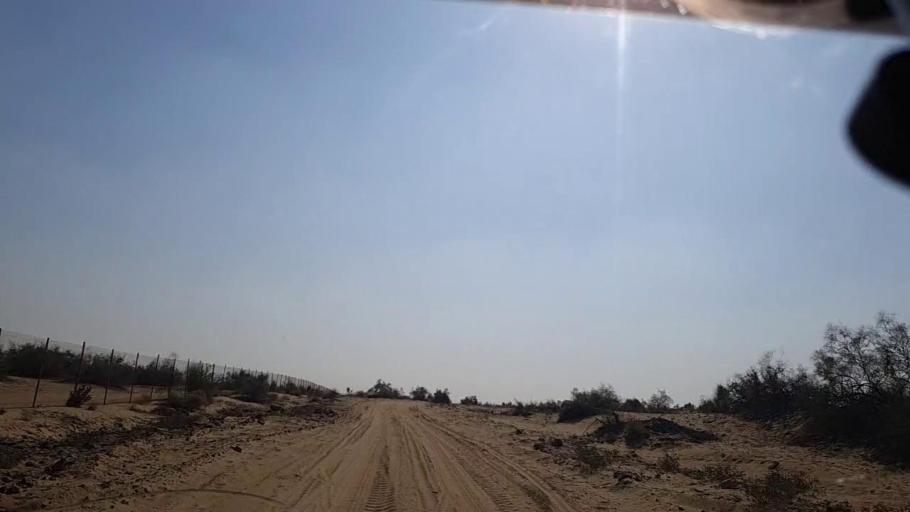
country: PK
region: Sindh
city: Khanpur
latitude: 27.5608
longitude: 69.3885
